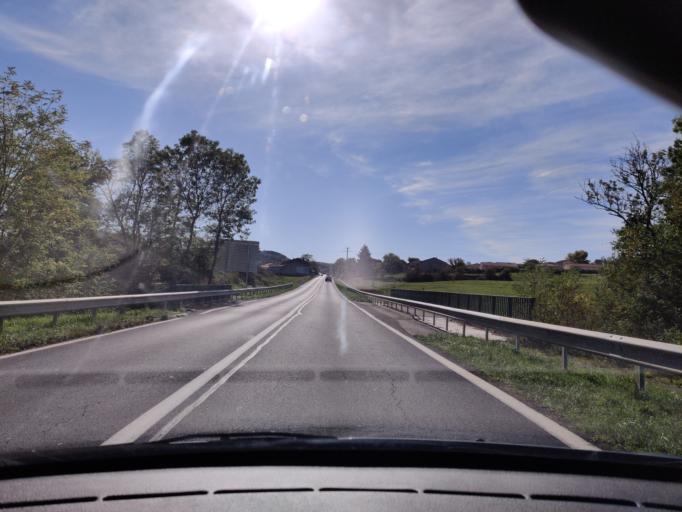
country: FR
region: Auvergne
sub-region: Departement du Puy-de-Dome
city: Combronde
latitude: 45.9909
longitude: 3.0881
